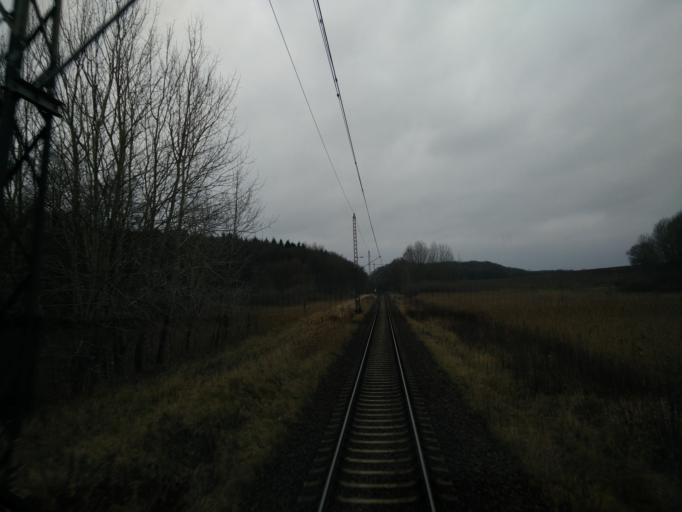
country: DE
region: Mecklenburg-Vorpommern
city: Bad Kleinen
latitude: 53.8081
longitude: 11.4812
